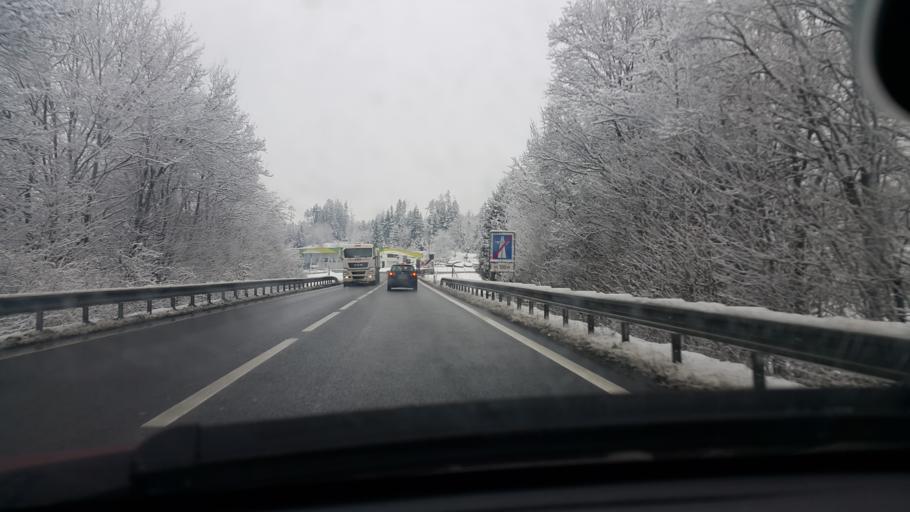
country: AT
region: Styria
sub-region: Politischer Bezirk Voitsberg
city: Mooskirchen
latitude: 47.0015
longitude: 15.2692
